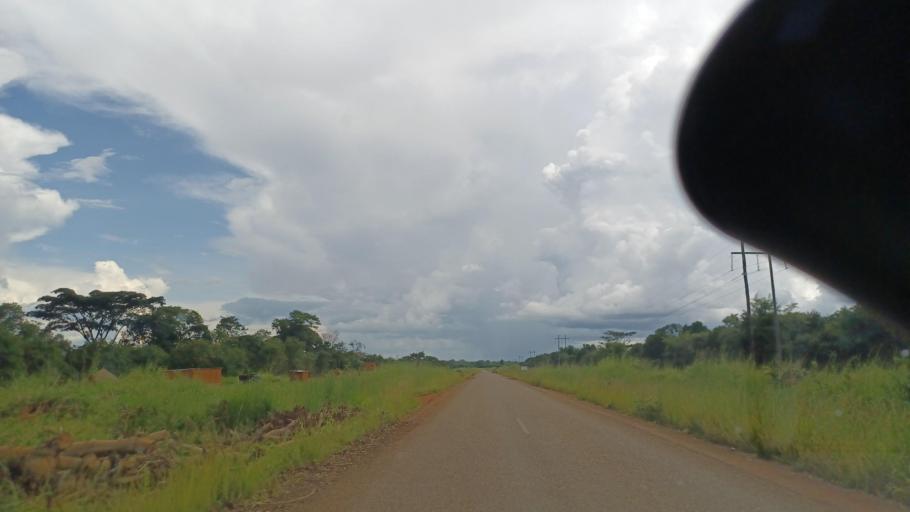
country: ZM
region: North-Western
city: Kasempa
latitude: -13.1152
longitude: 25.8699
